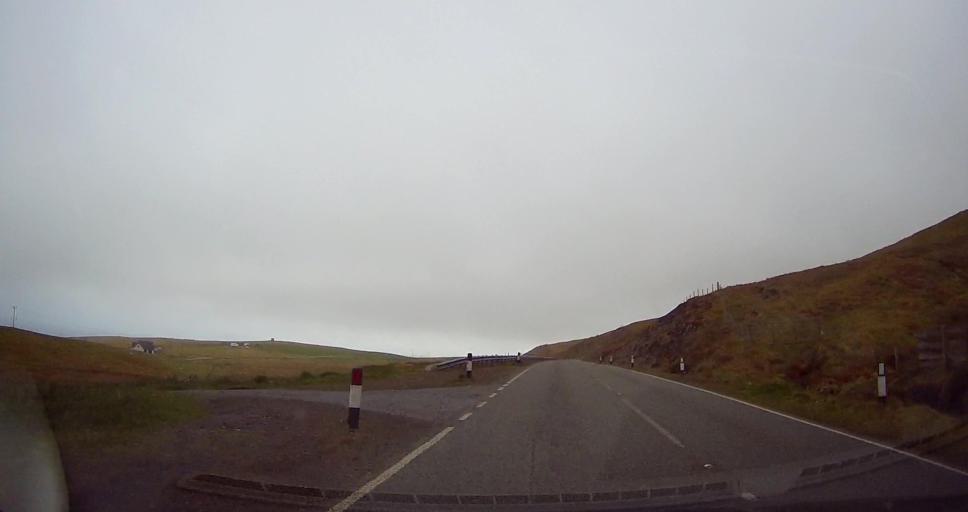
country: GB
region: Scotland
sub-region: Shetland Islands
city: Sandwick
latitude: 59.9683
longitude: -1.2805
